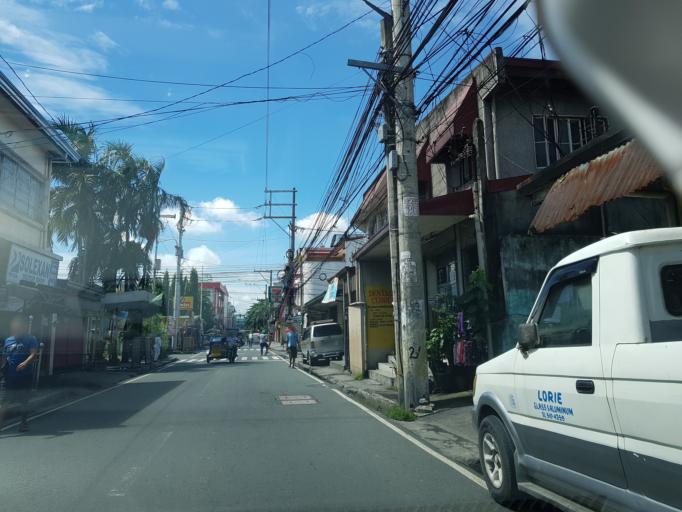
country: PH
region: Calabarzon
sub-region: Province of Rizal
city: Pateros
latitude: 14.5358
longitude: 121.0676
